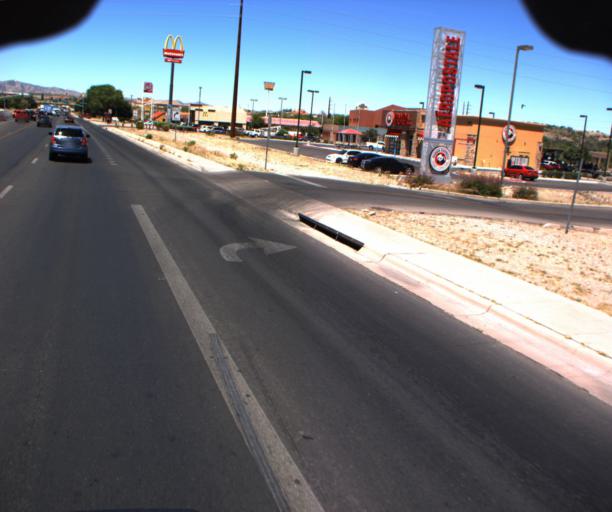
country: US
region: Arizona
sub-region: Santa Cruz County
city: Nogales
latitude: 31.3668
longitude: -110.9375
